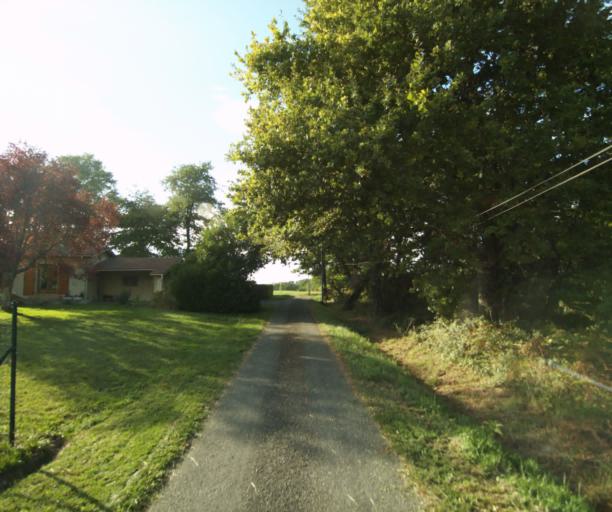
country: FR
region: Midi-Pyrenees
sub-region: Departement du Gers
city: Eauze
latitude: 43.8692
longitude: 0.0514
